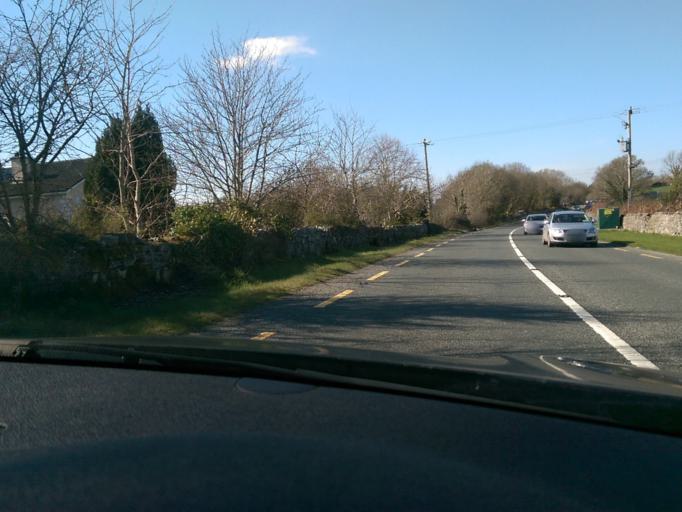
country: IE
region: Connaught
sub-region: County Galway
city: Moycullen
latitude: 53.3488
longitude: -9.1982
